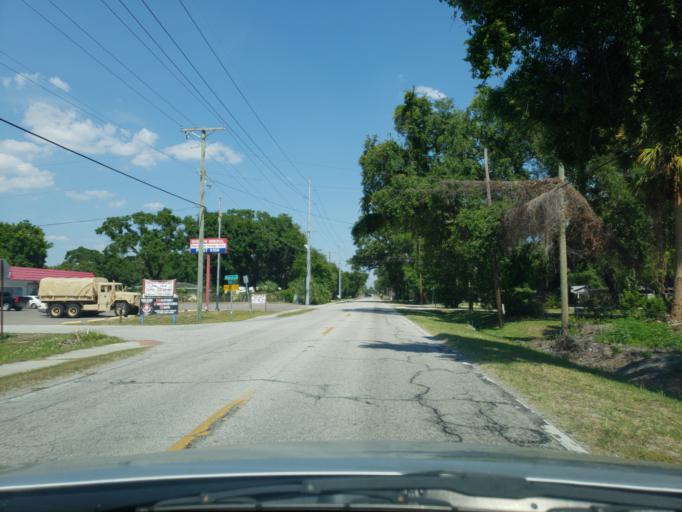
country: US
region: Florida
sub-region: Hillsborough County
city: Gibsonton
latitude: 27.8644
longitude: -82.3734
